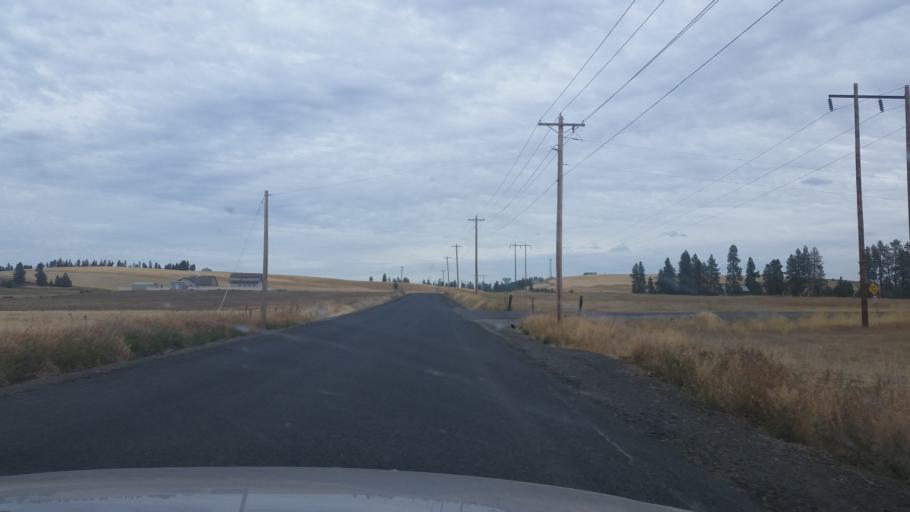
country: US
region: Washington
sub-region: Spokane County
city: Cheney
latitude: 47.5291
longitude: -117.5599
